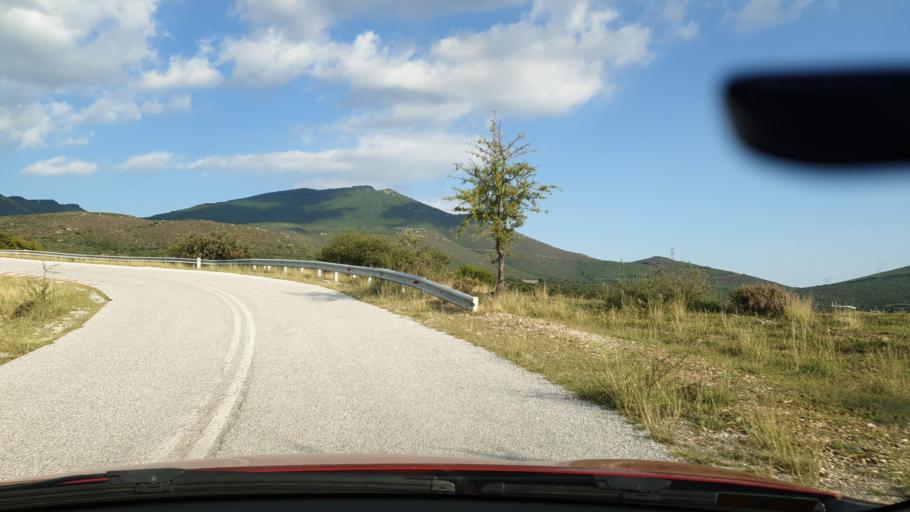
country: GR
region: Central Macedonia
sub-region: Nomos Thessalonikis
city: Peristera
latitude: 40.5138
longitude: 23.1726
